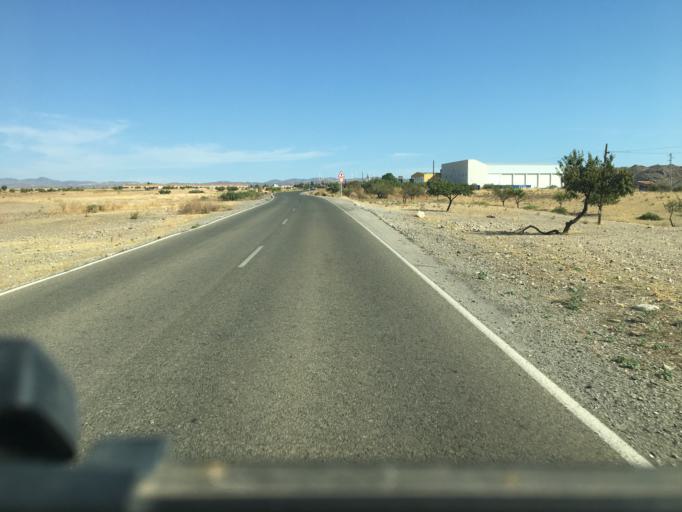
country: ES
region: Andalusia
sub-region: Provincia de Almeria
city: Huercal-Overa
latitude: 37.4378
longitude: -1.9759
